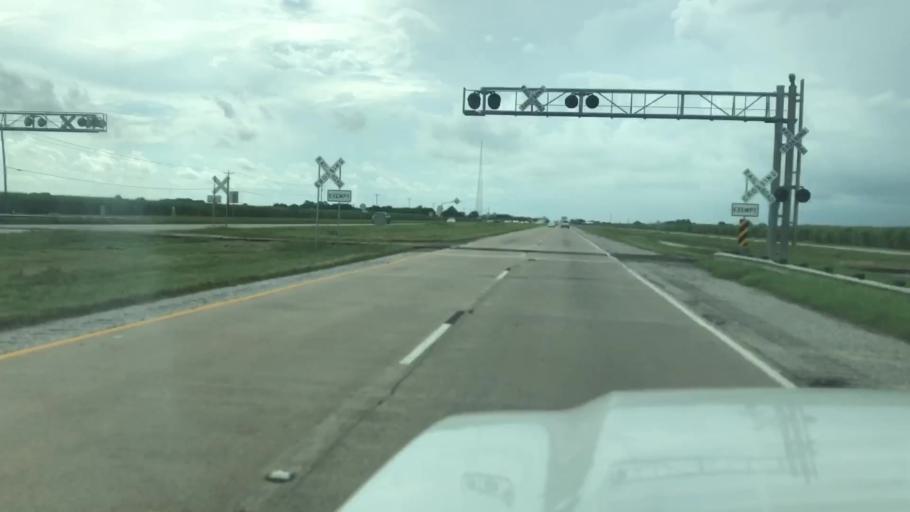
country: US
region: Louisiana
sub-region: Iberia Parish
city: Jeanerette
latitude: 29.9123
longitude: -91.7172
